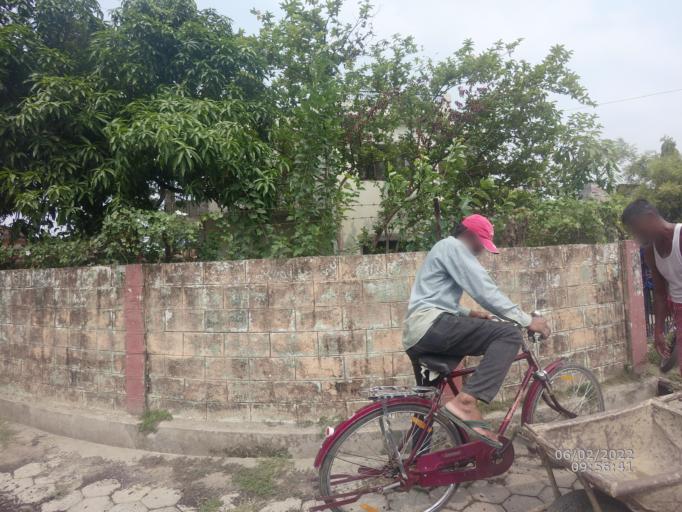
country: NP
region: Western Region
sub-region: Lumbini Zone
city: Bhairahawa
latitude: 27.5021
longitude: 83.4549
